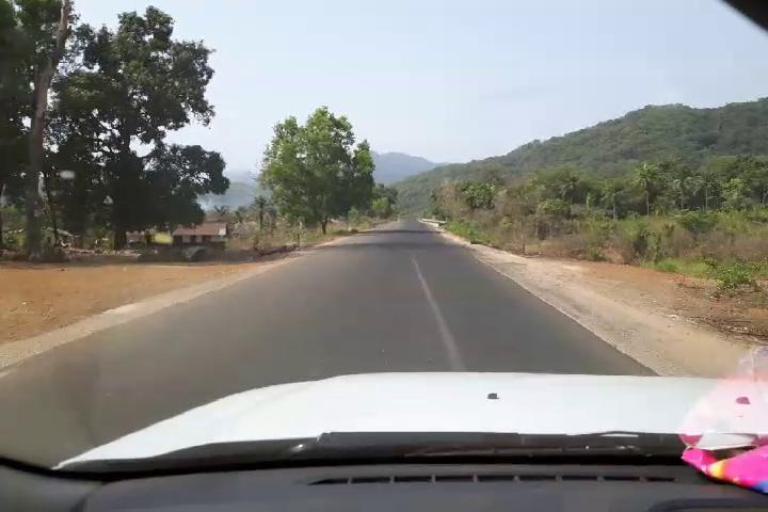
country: SL
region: Western Area
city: Hastings
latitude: 8.2732
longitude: -13.1578
